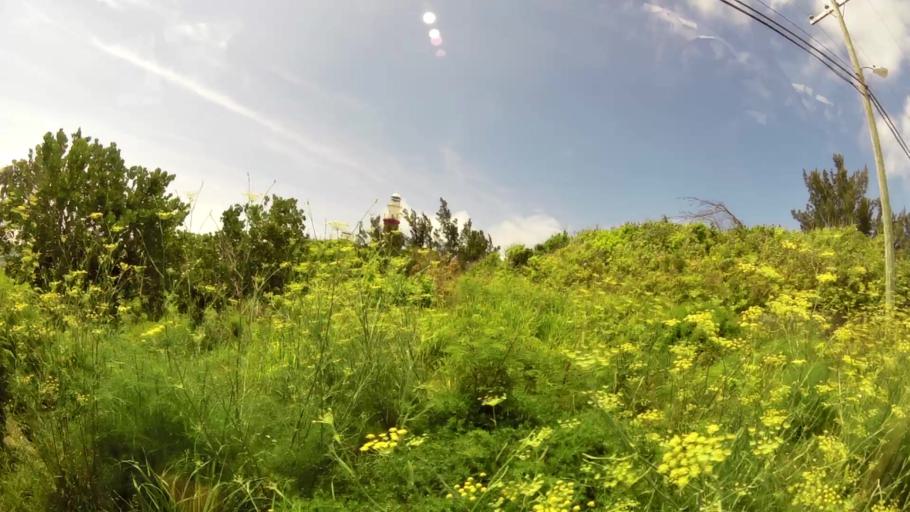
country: BM
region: Saint George
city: Saint George
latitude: 32.3652
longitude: -64.6525
